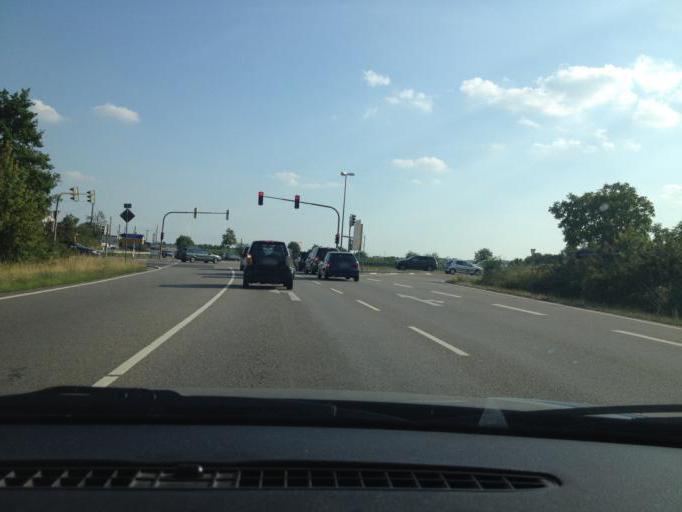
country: DE
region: Rheinland-Pfalz
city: Neustadt
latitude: 49.3396
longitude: 8.1508
